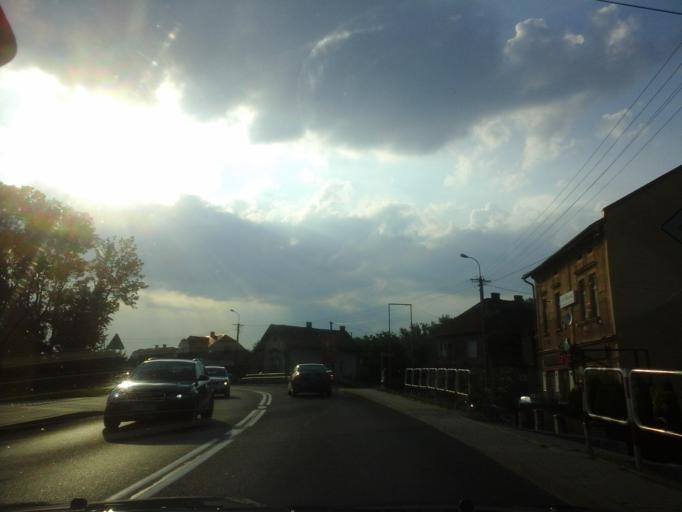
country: PL
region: Lesser Poland Voivodeship
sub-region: Powiat wadowicki
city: Brzeznica
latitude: 49.9660
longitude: 19.6333
